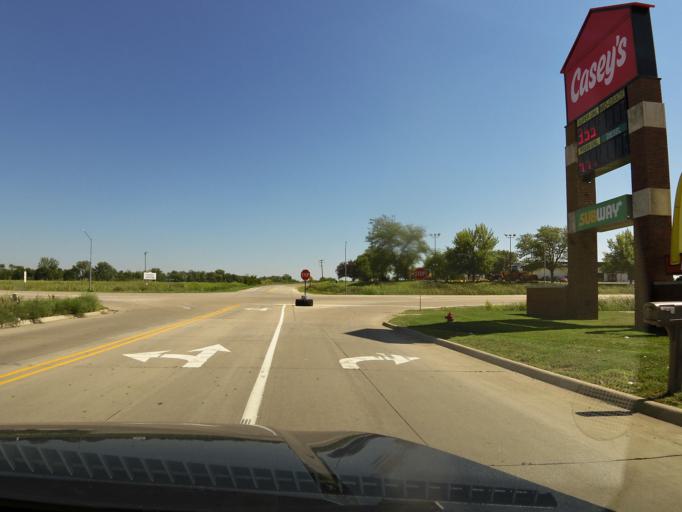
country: US
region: Iowa
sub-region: Linn County
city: Center Point
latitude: 42.1732
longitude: -91.7765
